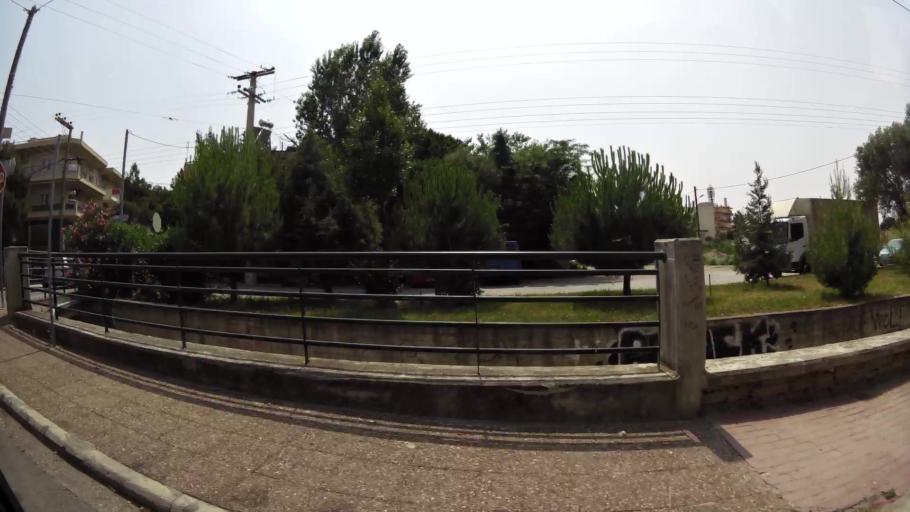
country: GR
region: Central Macedonia
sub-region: Nomos Thessalonikis
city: Diavata
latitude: 40.6884
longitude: 22.8539
